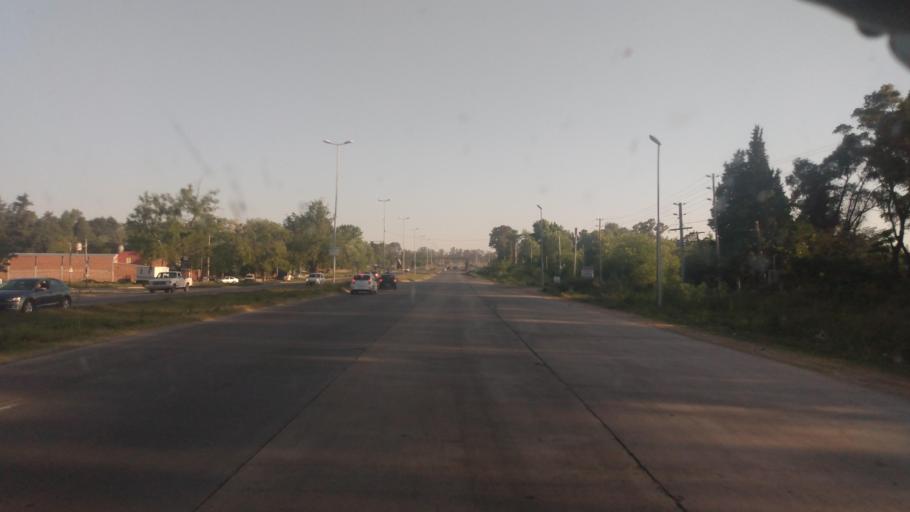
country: AR
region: Buenos Aires
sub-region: Partido de Campana
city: Campana
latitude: -34.2475
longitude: -58.9658
